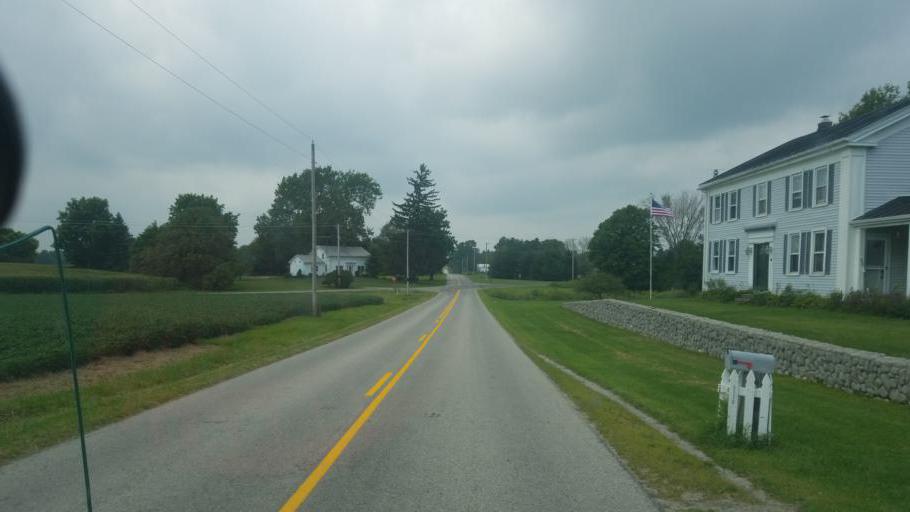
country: US
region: Ohio
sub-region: Huron County
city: Greenwich
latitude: 41.0806
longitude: -82.5614
